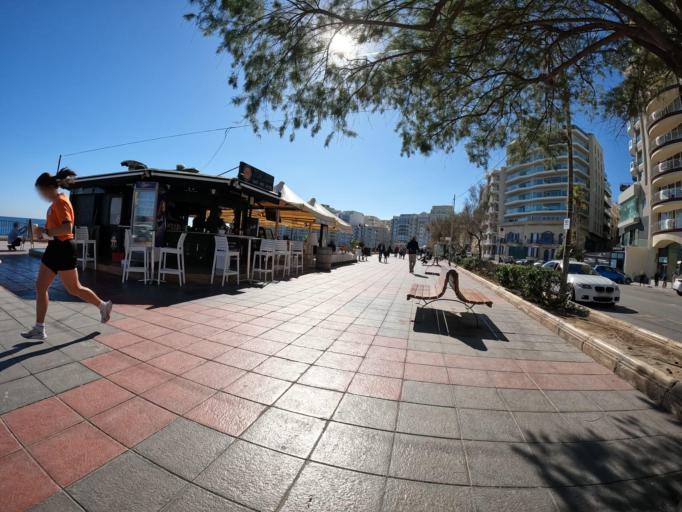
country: MT
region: Tas-Sliema
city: Sliema
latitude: 35.9136
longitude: 14.5069
